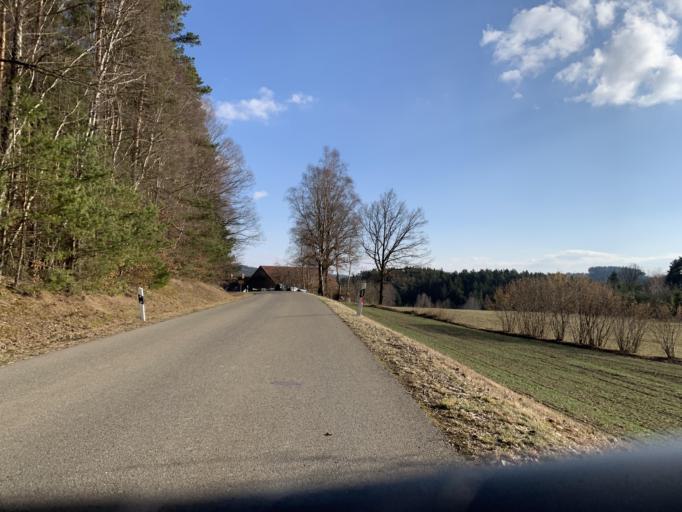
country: DE
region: Bavaria
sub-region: Upper Palatinate
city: Thanstein
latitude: 49.3714
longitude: 12.4359
